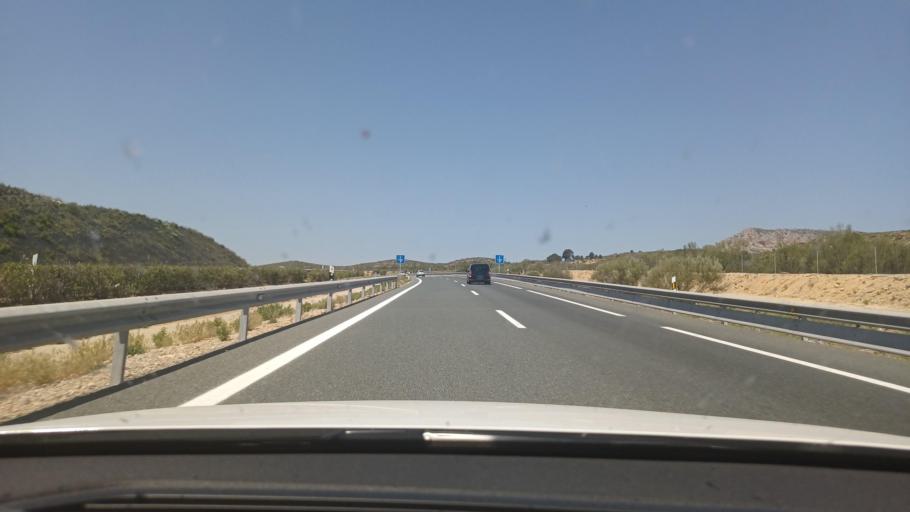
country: ES
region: Castille-La Mancha
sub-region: Provincia de Albacete
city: Almansa
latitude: 38.8794
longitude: -1.1609
